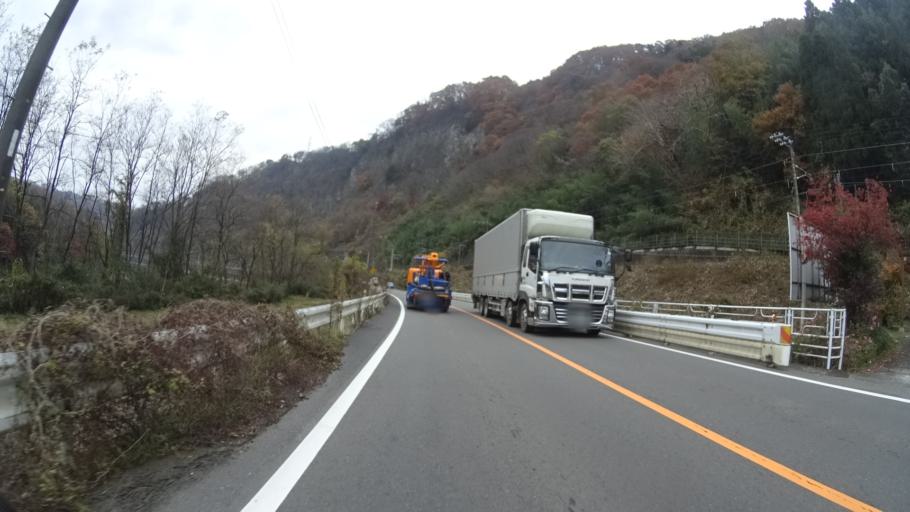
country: JP
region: Gunma
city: Numata
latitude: 36.5949
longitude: 139.0492
